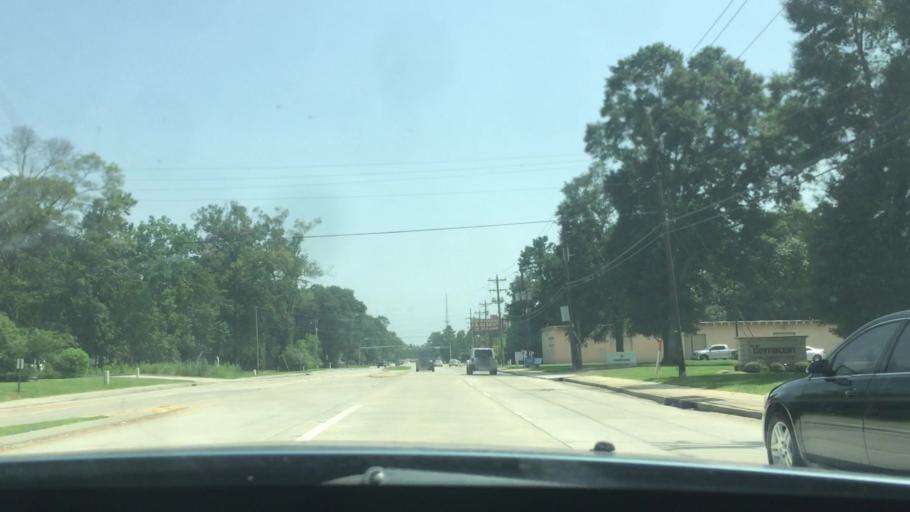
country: US
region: Louisiana
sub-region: East Baton Rouge Parish
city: Shenandoah
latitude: 30.4283
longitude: -91.0076
